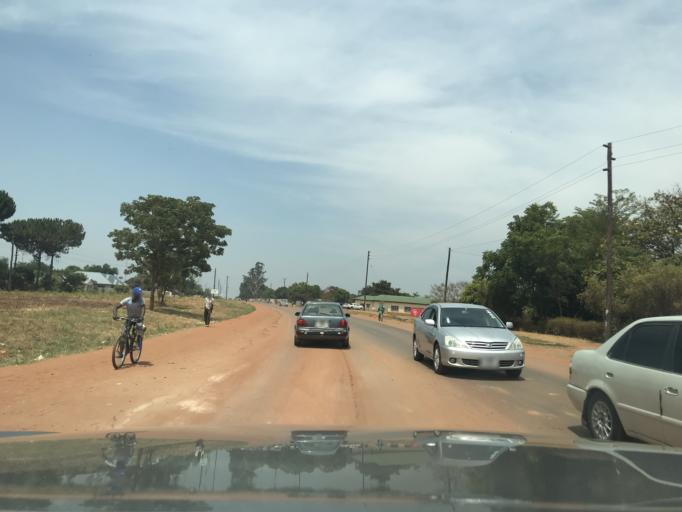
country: ZM
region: Northern
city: Kasama
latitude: -10.2051
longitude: 31.1804
